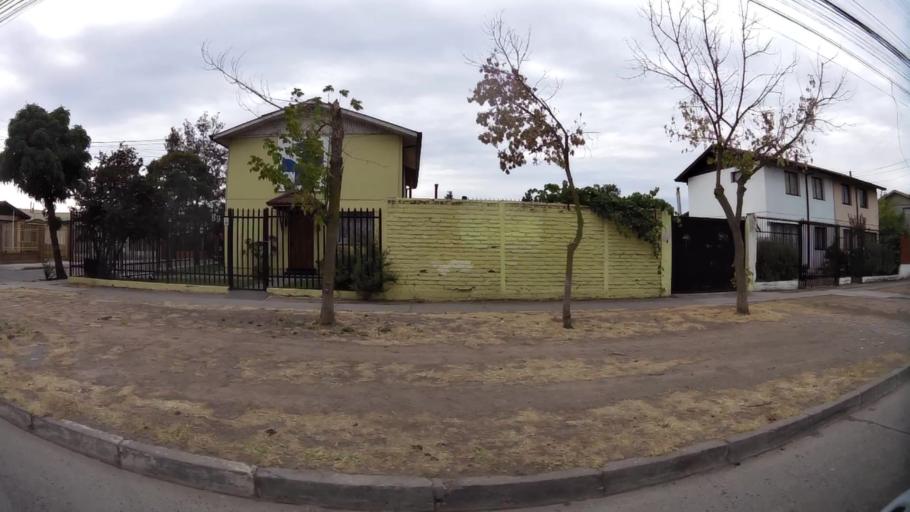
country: CL
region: O'Higgins
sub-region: Provincia de Cachapoal
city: Rancagua
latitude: -34.1609
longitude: -70.7346
